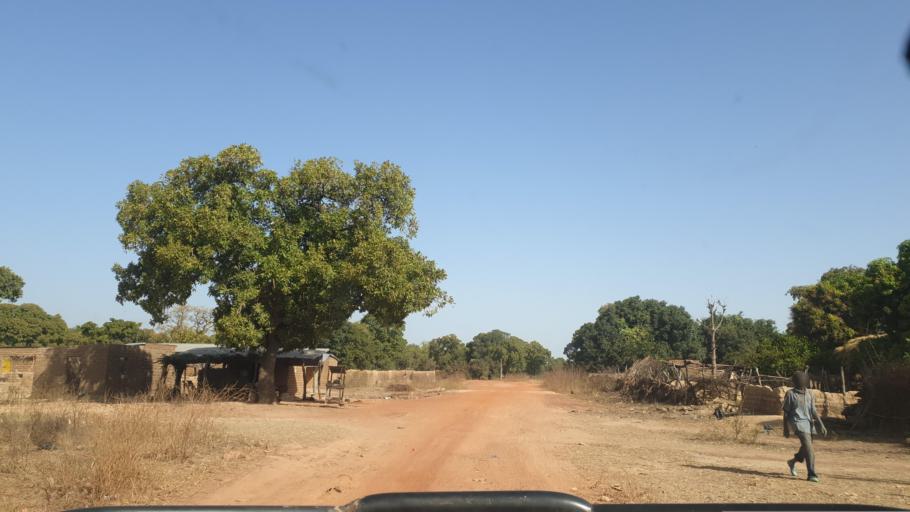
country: ML
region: Sikasso
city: Bougouni
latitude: 11.7695
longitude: -6.9025
